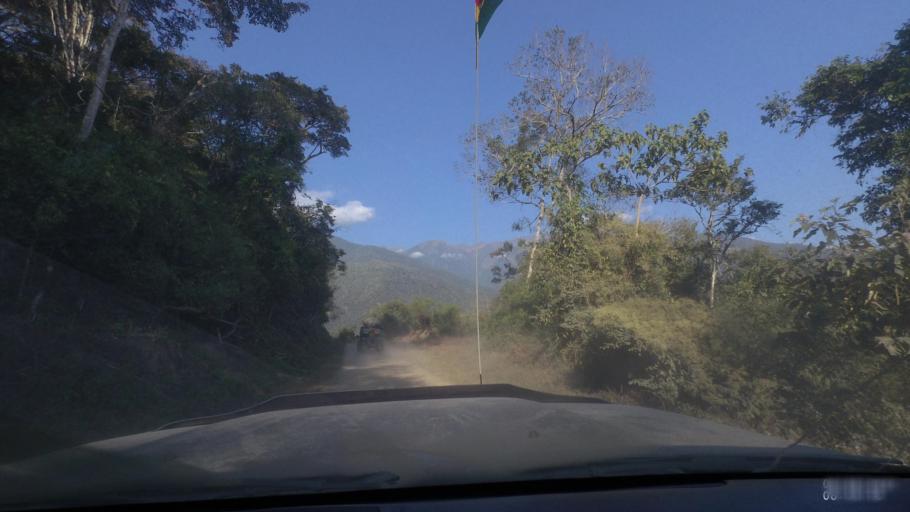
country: BO
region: La Paz
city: Quime
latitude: -16.5197
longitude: -66.7700
